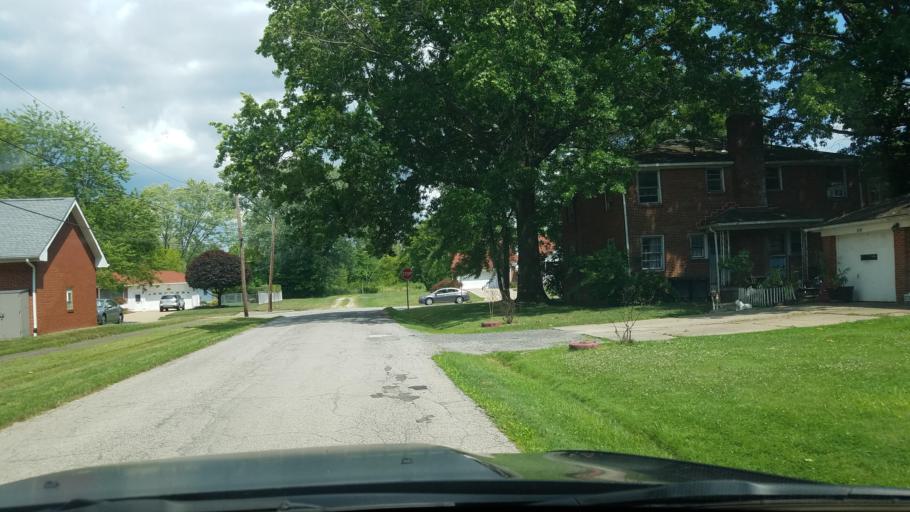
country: US
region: Ohio
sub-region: Trumbull County
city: Bolindale
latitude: 41.2279
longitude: -80.7790
